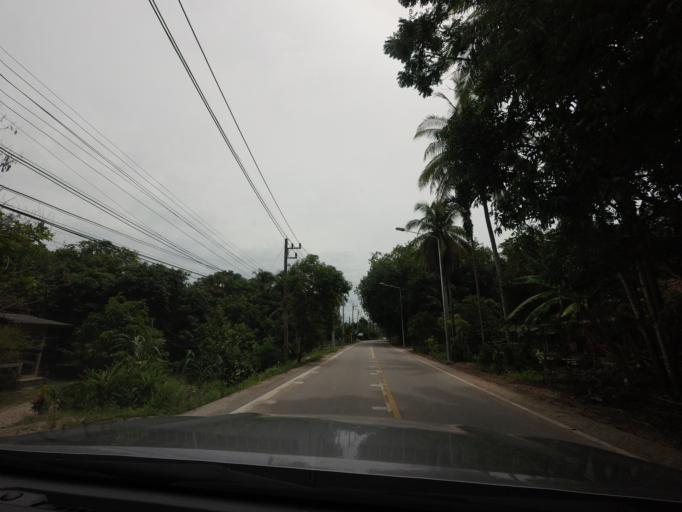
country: TH
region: Pattani
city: Kapho
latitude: 6.5745
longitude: 101.5350
